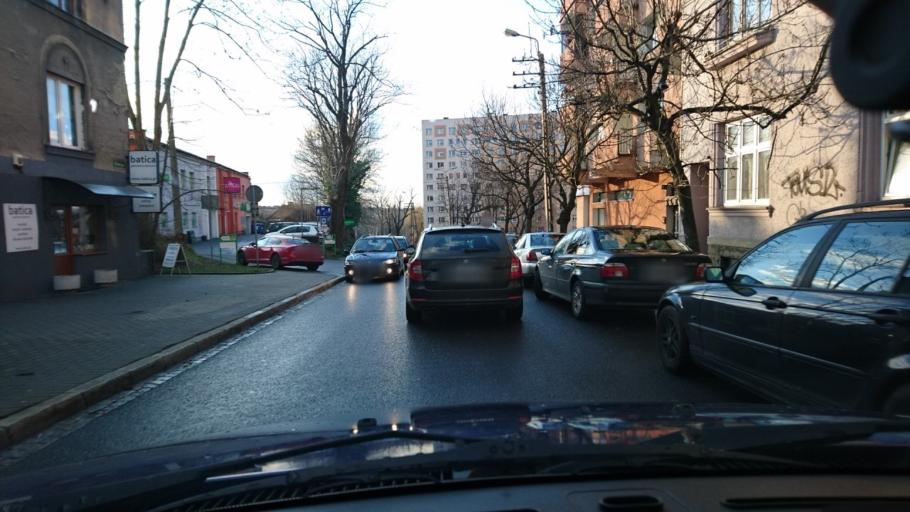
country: PL
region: Silesian Voivodeship
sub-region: Bielsko-Biala
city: Bielsko-Biala
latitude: 49.8216
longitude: 19.0268
